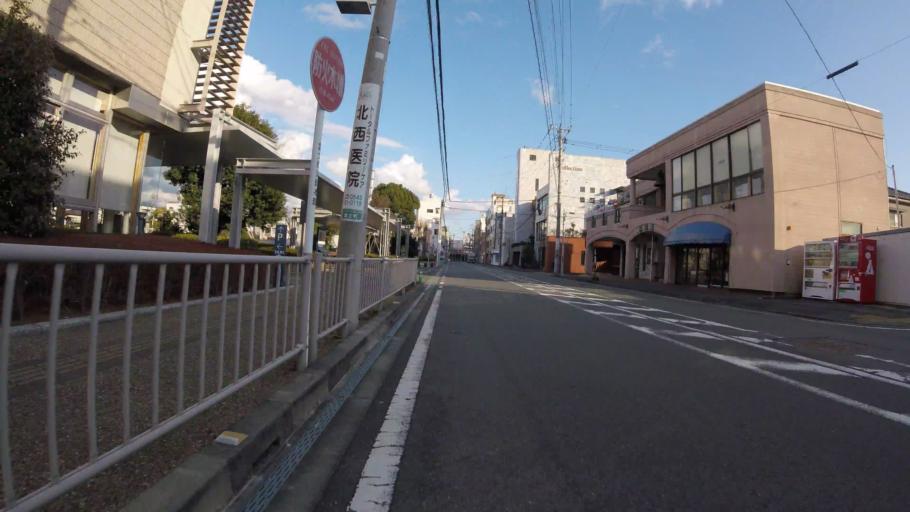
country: JP
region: Shizuoka
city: Fuji
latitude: 35.1540
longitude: 138.6487
